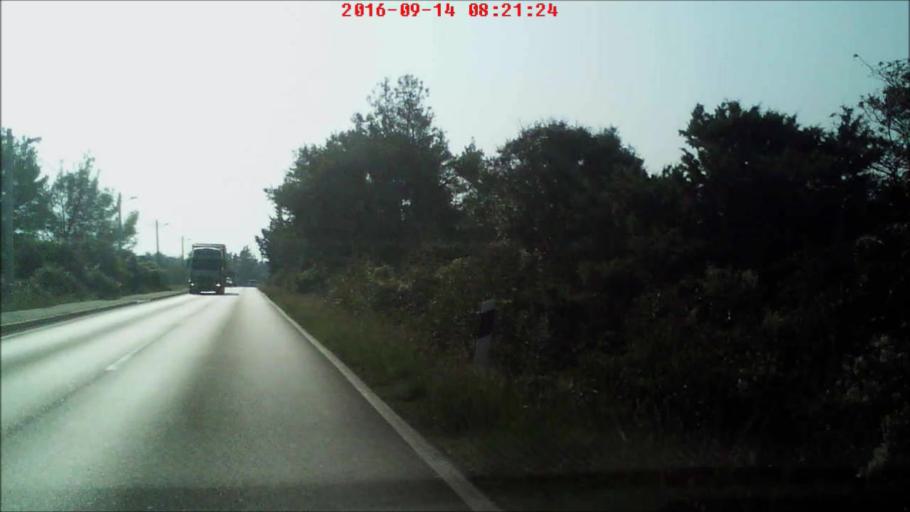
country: HR
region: Zadarska
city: Nin
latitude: 44.2223
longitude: 15.2108
